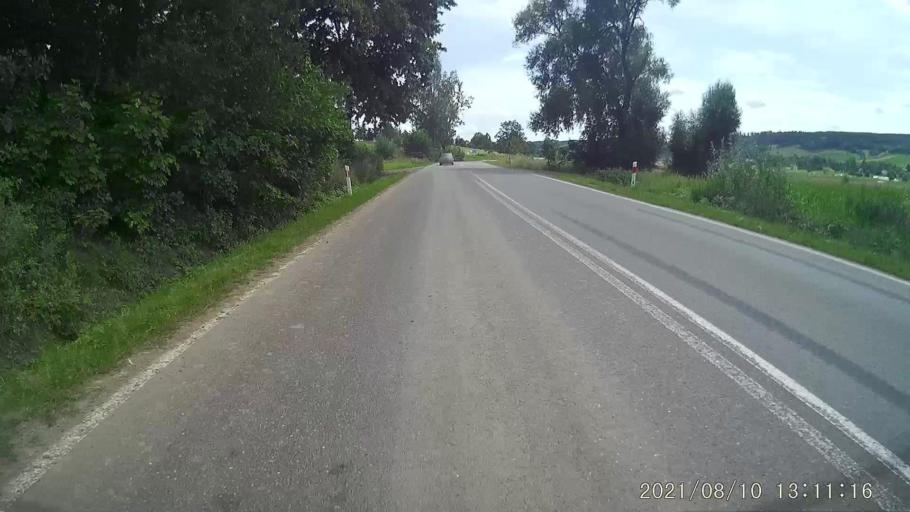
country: PL
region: Lower Silesian Voivodeship
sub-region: Powiat klodzki
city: Bozkow
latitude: 50.5068
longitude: 16.5227
